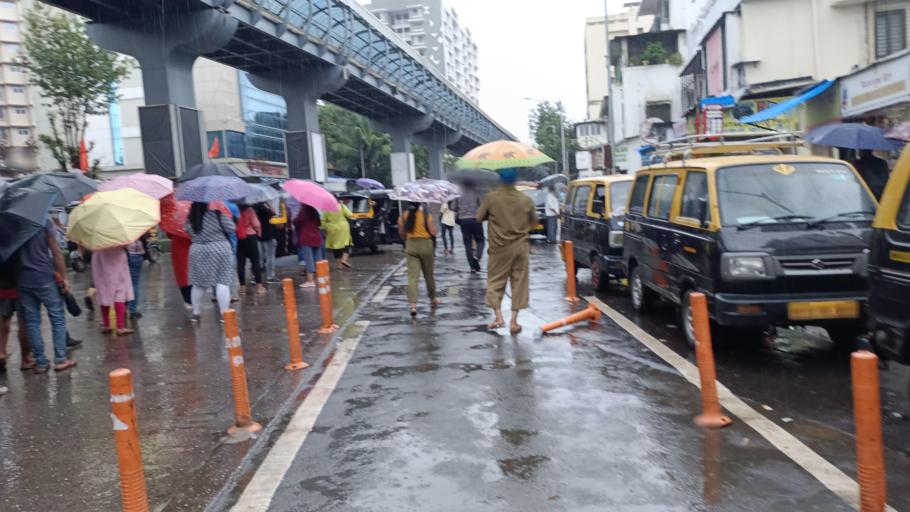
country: IN
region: Maharashtra
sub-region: Mumbai Suburban
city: Powai
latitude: 19.1183
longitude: 72.8480
